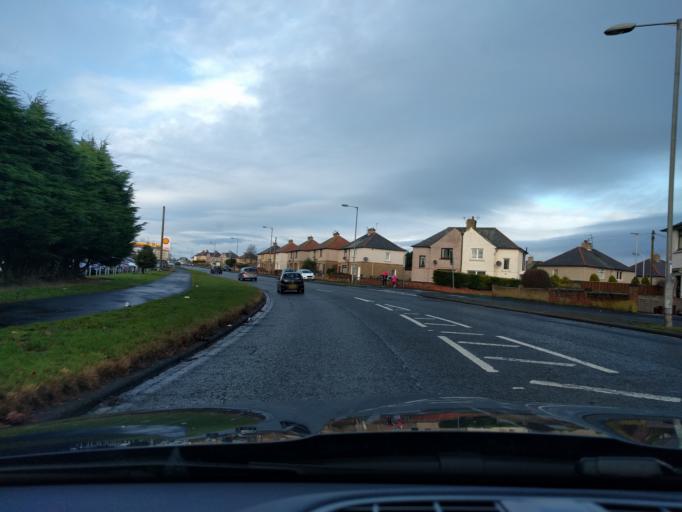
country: GB
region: England
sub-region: Northumberland
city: Berwick-Upon-Tweed
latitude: 55.7805
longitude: -2.0105
